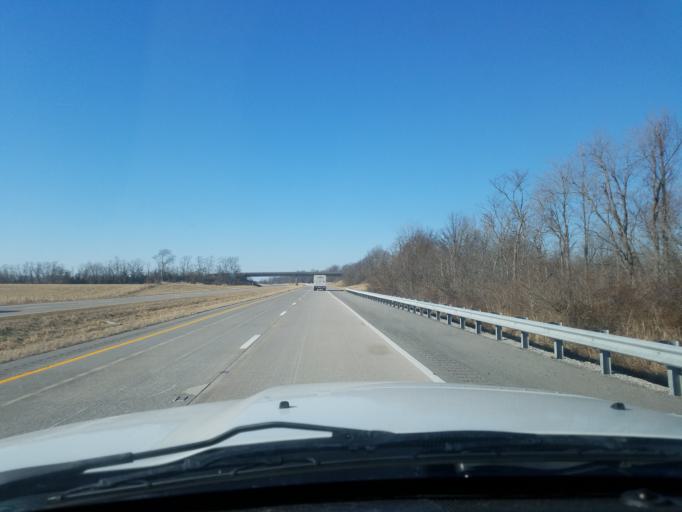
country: US
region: Kentucky
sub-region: Henderson County
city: Henderson
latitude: 37.7693
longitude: -87.4279
